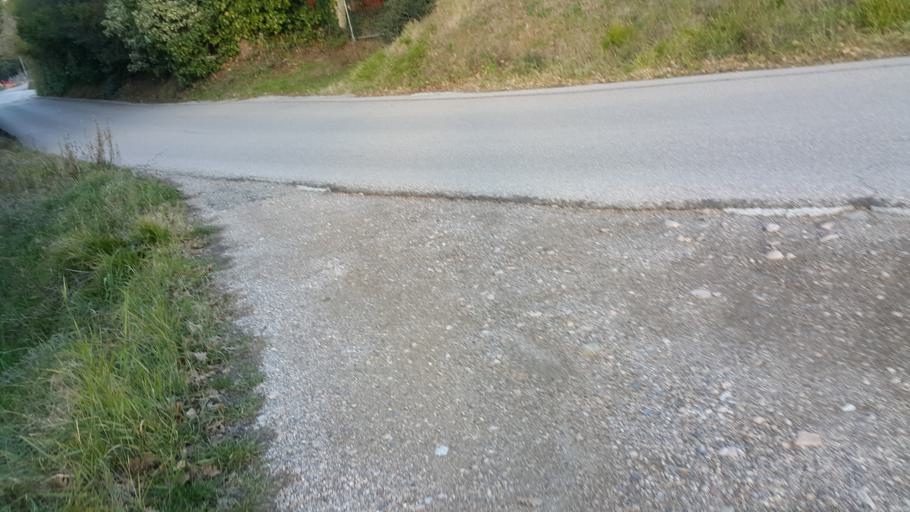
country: IT
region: Umbria
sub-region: Provincia di Perugia
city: Perugia
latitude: 43.0894
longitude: 12.3762
